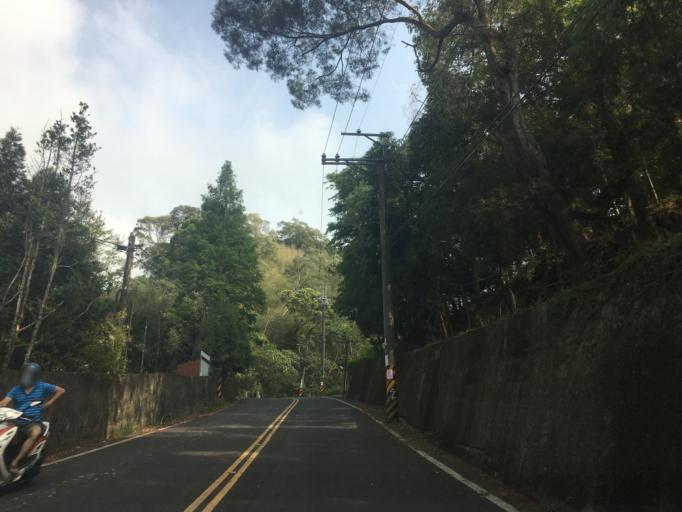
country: TW
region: Taiwan
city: Fengyuan
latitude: 24.2262
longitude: 120.7548
